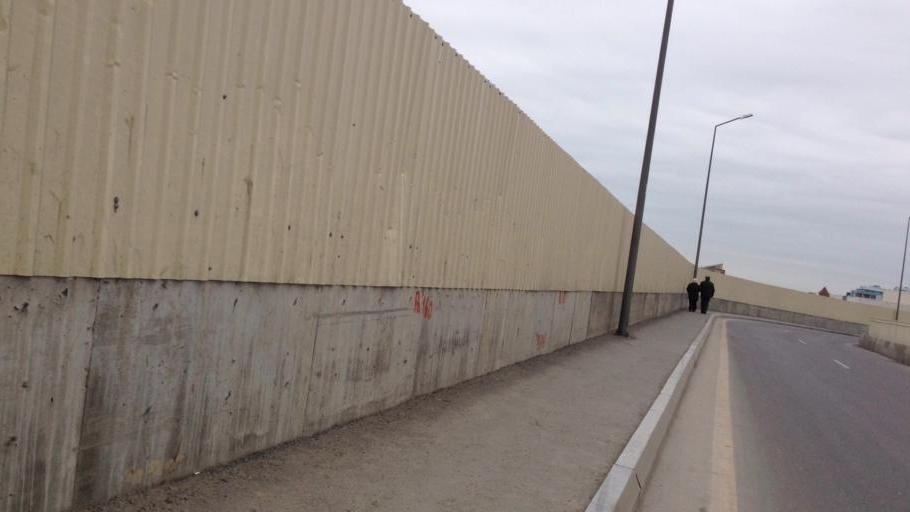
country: AZ
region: Baki
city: Baku
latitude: 40.3984
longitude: 49.8498
